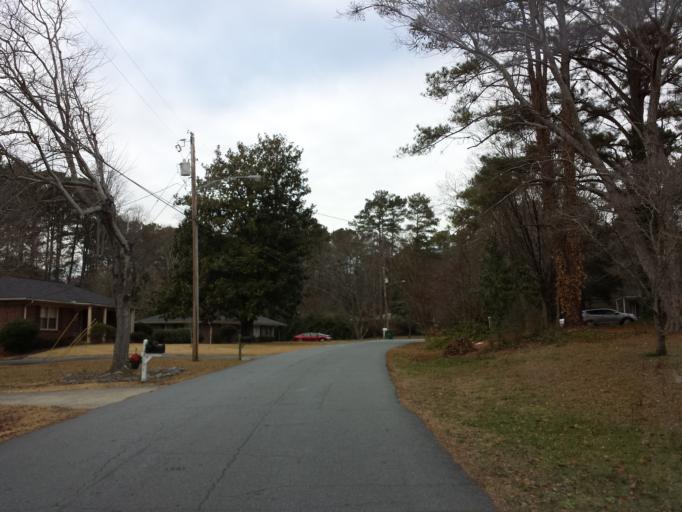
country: US
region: Georgia
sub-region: Cobb County
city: Fair Oaks
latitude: 33.9425
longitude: -84.4895
